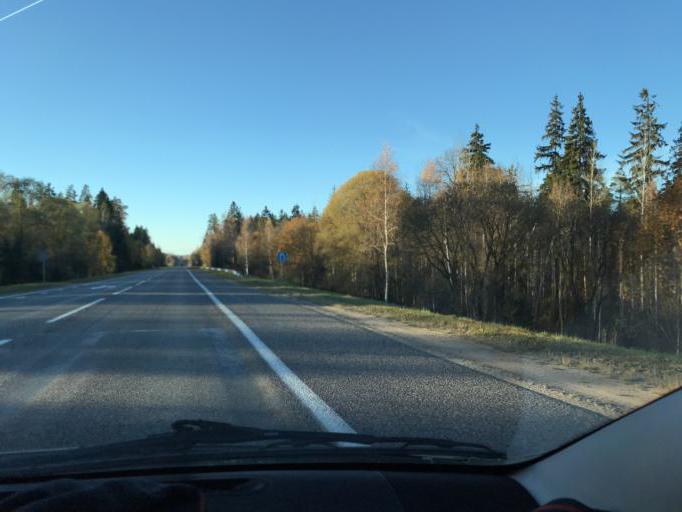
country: BY
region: Vitebsk
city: Vitebsk
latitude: 55.3405
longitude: 30.2350
